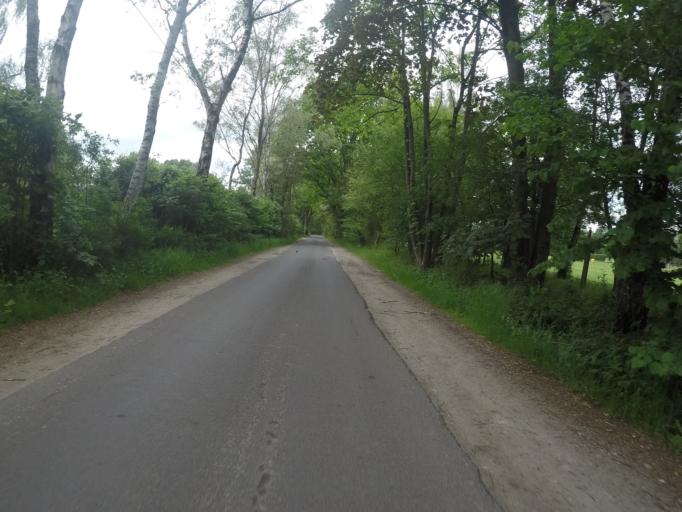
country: DE
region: Schleswig-Holstein
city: Bonningstedt
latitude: 53.6529
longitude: 9.9403
